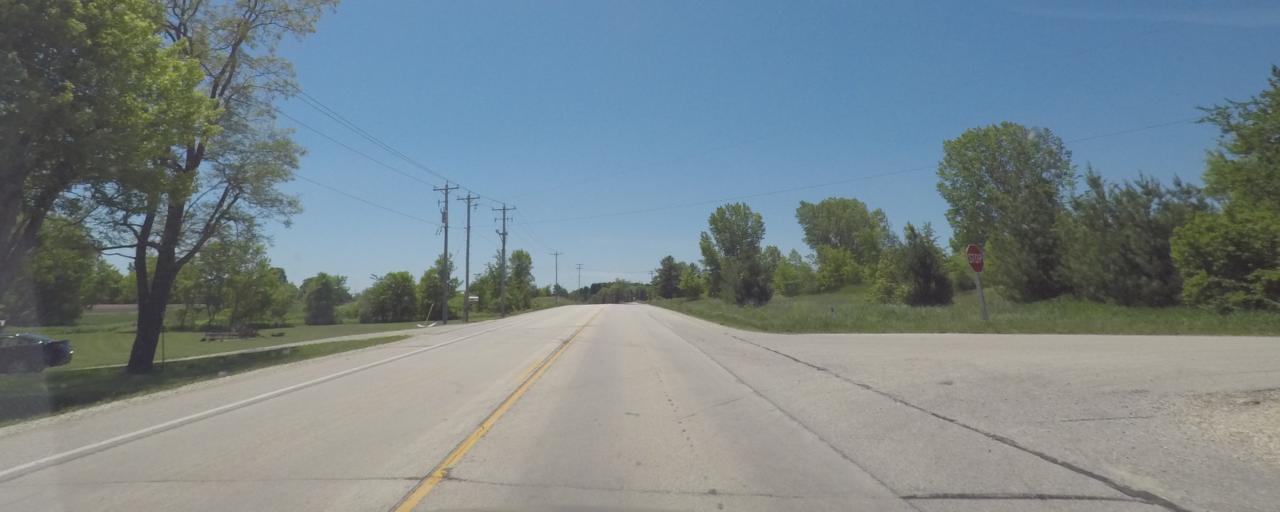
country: US
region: Wisconsin
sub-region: Ozaukee County
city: Kohler
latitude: 43.5382
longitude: -88.0902
